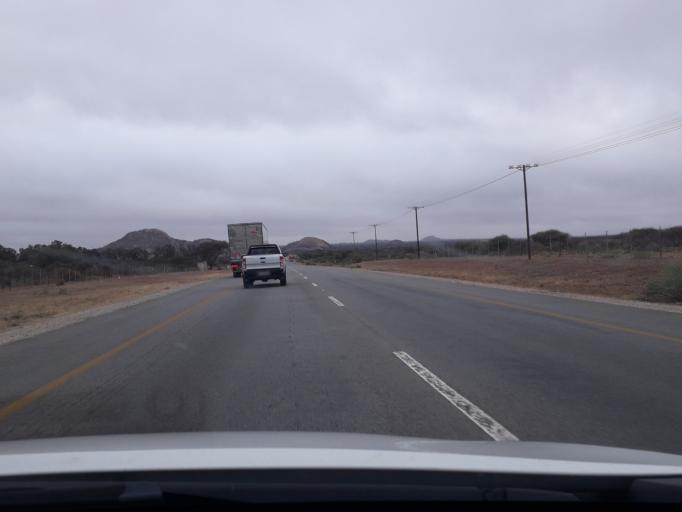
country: ZA
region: Limpopo
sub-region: Capricorn District Municipality
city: Mankoeng
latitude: -23.5483
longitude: 29.6919
